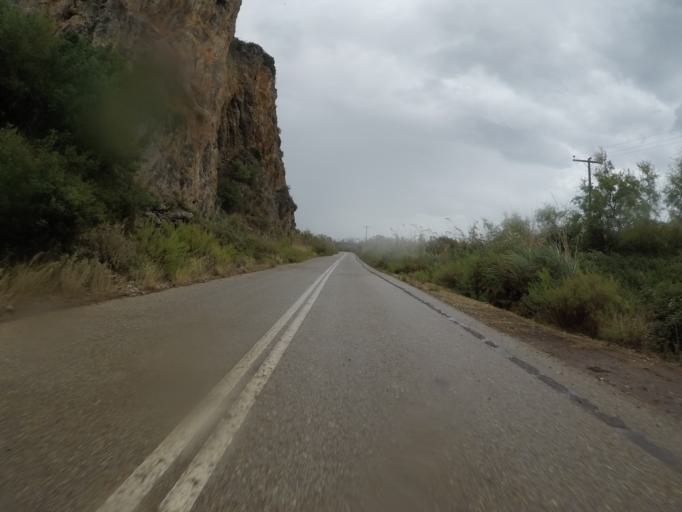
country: GR
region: West Greece
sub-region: Nomos Ileias
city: Zacharo
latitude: 37.5231
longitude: 21.5966
